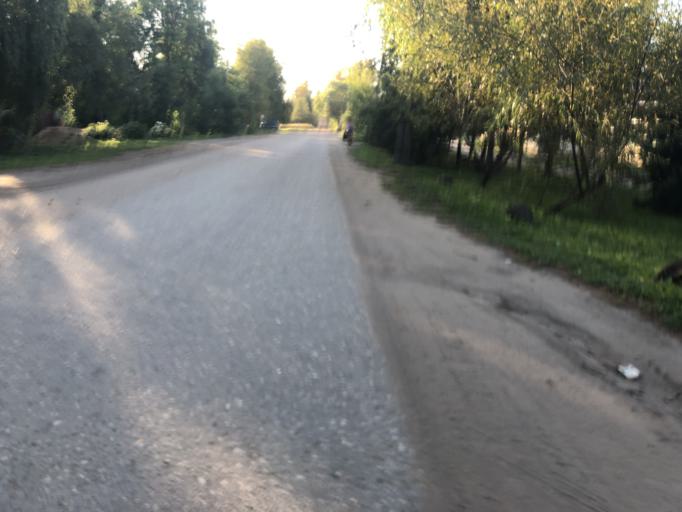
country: RU
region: Tverskaya
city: Rzhev
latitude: 56.2427
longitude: 34.3150
